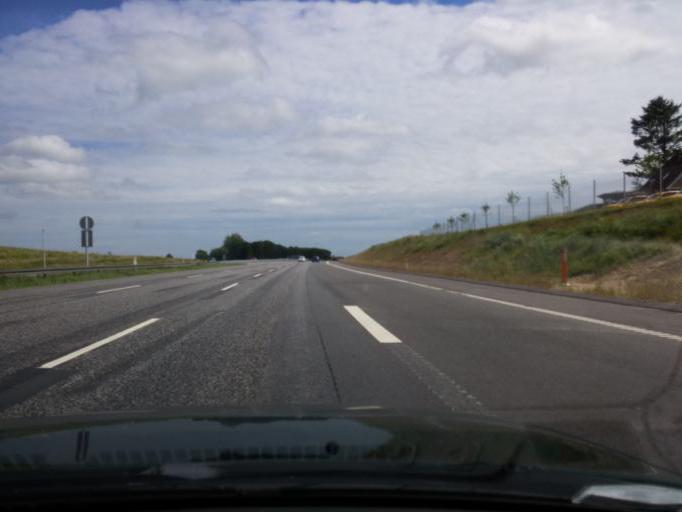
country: DK
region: South Denmark
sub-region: Middelfart Kommune
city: Strib
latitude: 55.5128
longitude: 9.7744
